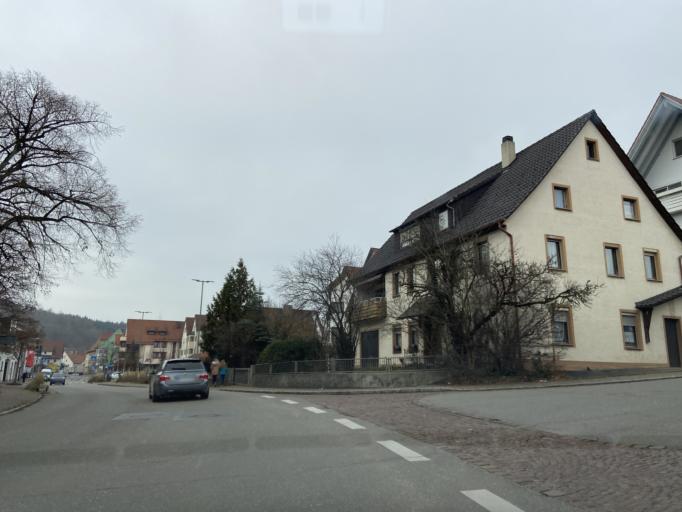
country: DE
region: Baden-Wuerttemberg
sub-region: Tuebingen Region
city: Gammertingen
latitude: 48.2496
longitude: 9.2184
